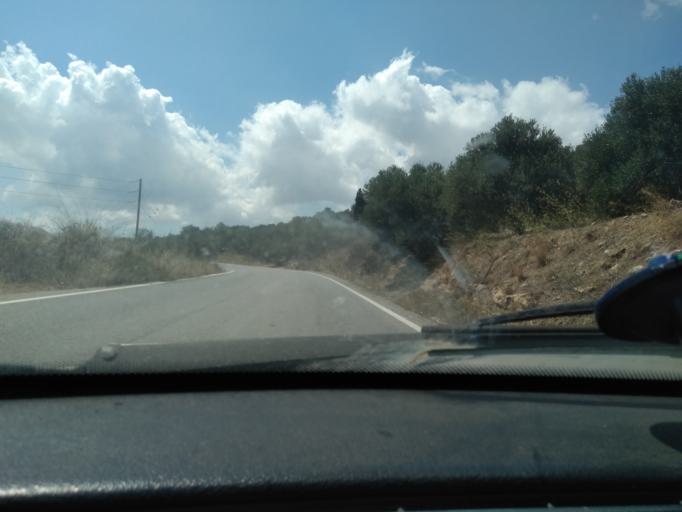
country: GR
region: Crete
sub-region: Nomos Lasithiou
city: Siteia
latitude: 35.1377
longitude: 26.0755
